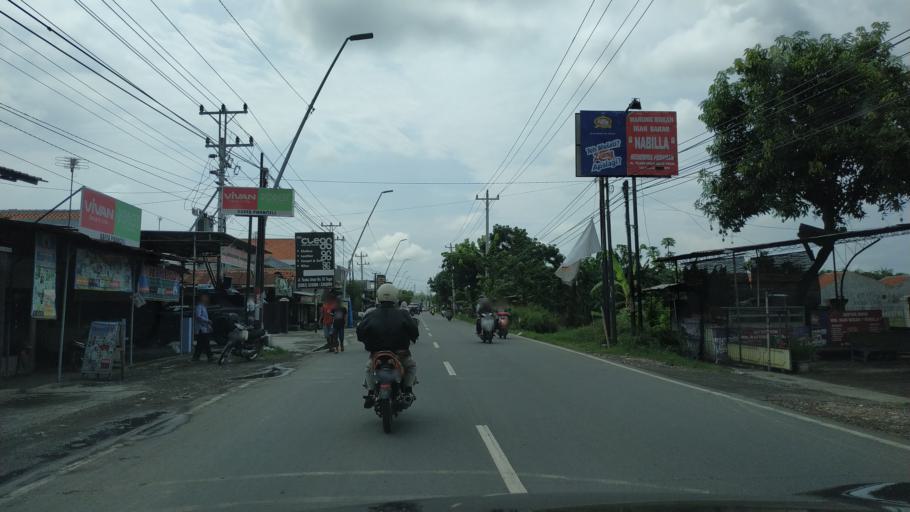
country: ID
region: Central Java
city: Tegal
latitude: -6.8871
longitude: 109.1264
